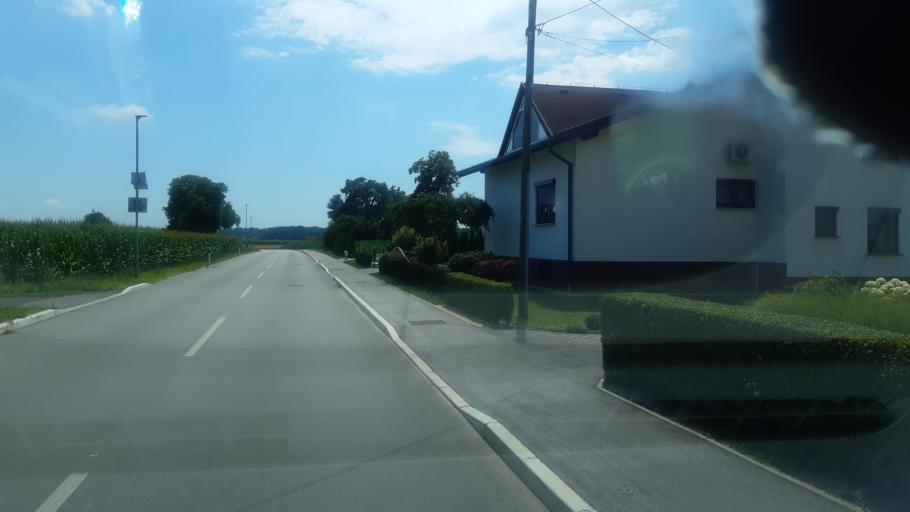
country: SI
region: Moravske Toplice
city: Moravske Toplice
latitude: 46.6820
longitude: 16.1944
